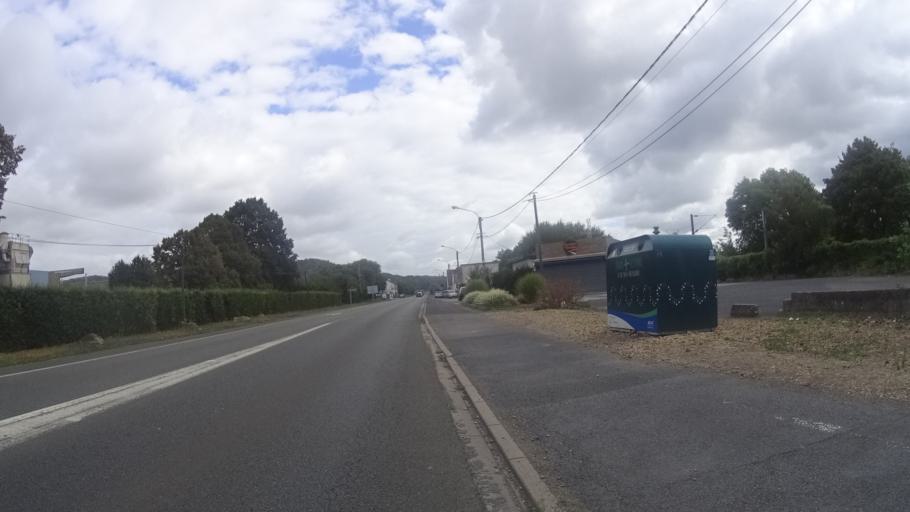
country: FR
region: Picardie
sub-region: Departement de l'Oise
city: Clairoix
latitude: 49.4328
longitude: 2.8403
